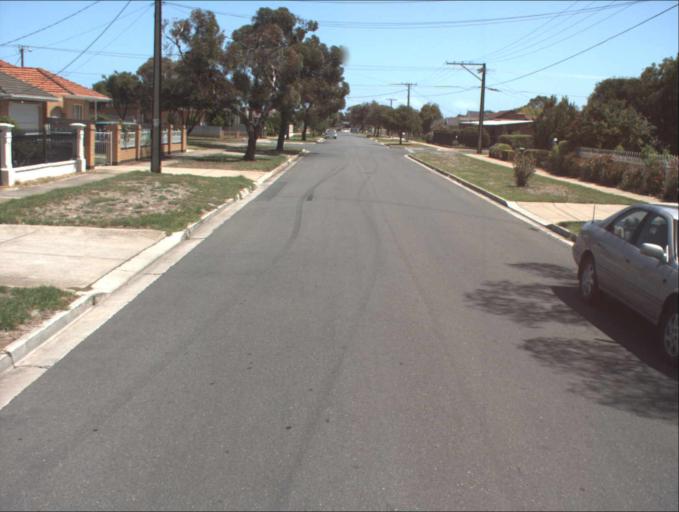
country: AU
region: South Australia
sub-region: Charles Sturt
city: Woodville North
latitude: -34.8617
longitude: 138.5650
